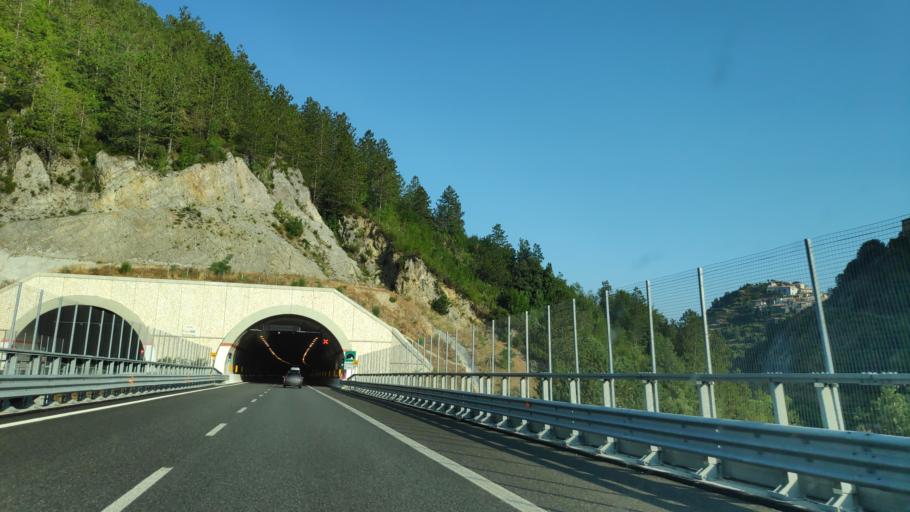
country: IT
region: Calabria
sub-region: Provincia di Cosenza
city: Mormanno
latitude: 39.8799
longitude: 15.9874
